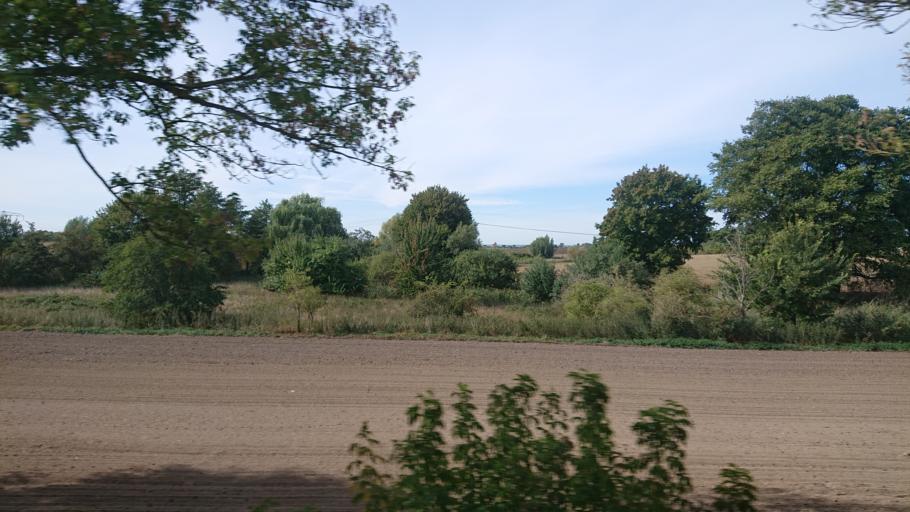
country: DE
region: Brandenburg
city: Gramzow
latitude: 53.2490
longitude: 13.9648
